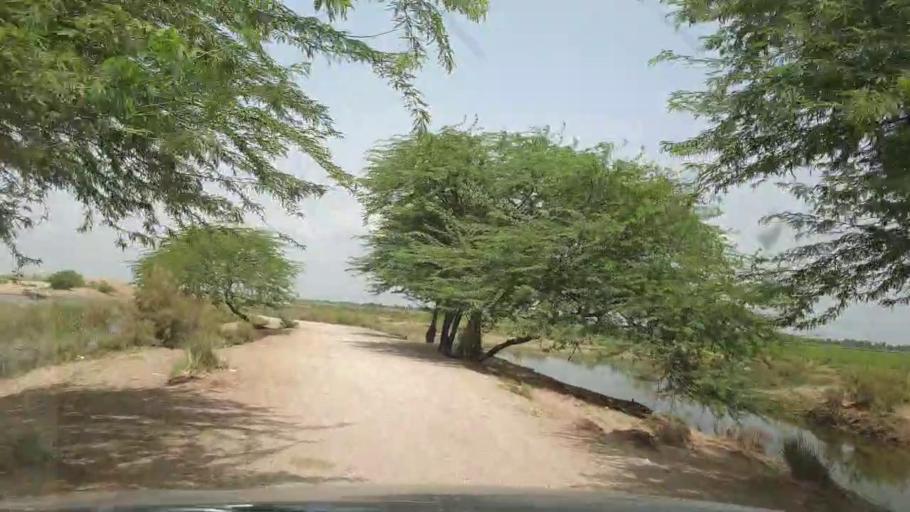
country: PK
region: Sindh
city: Ratodero
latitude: 27.9106
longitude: 68.3024
